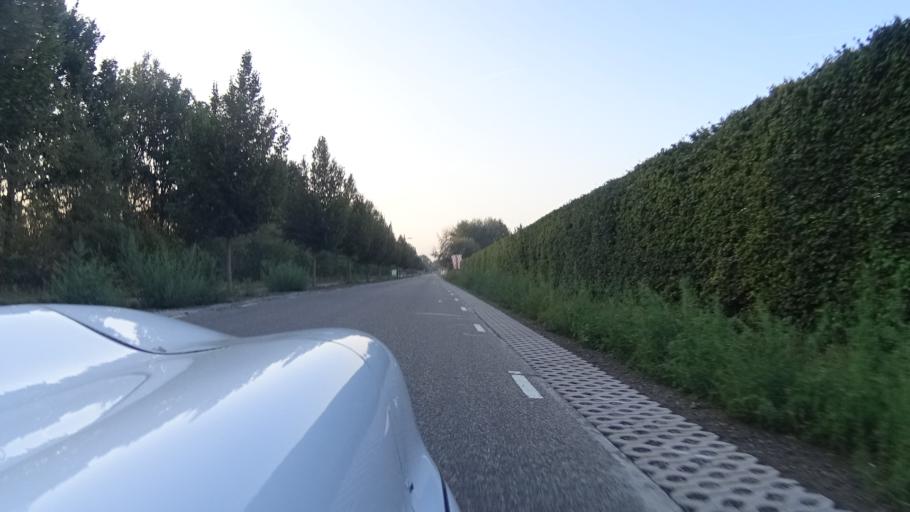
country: NL
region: North Brabant
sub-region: Gemeente Sint Anthonis
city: Sint Anthonis
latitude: 51.6093
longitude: 5.9093
